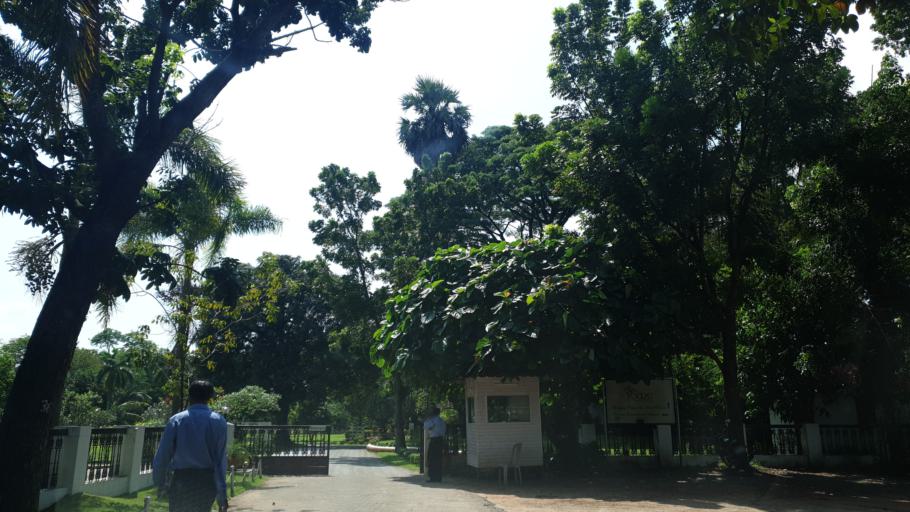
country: IN
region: Kerala
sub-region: Ernakulam
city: Cochin
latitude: 9.9852
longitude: 76.2674
